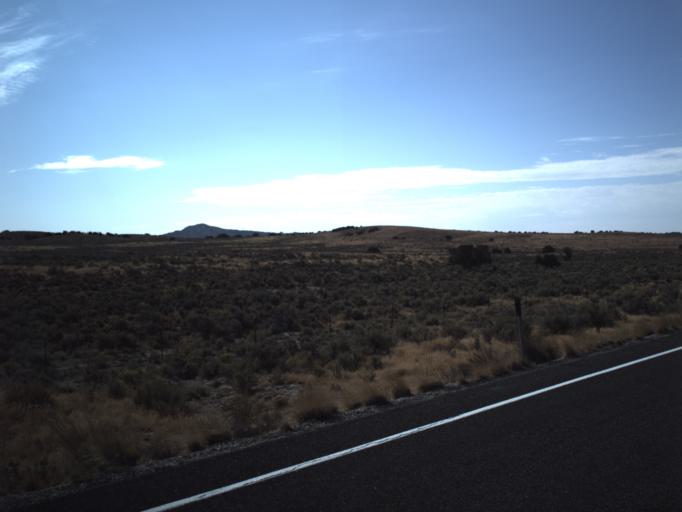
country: US
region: Idaho
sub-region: Cassia County
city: Burley
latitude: 41.6961
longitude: -113.5353
